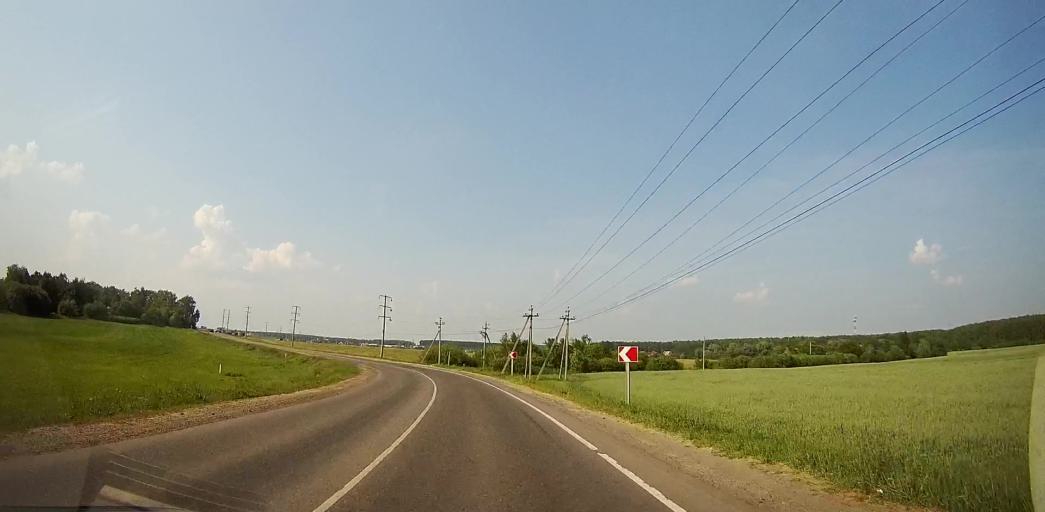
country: RU
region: Moskovskaya
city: Barybino
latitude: 55.2609
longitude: 37.9192
